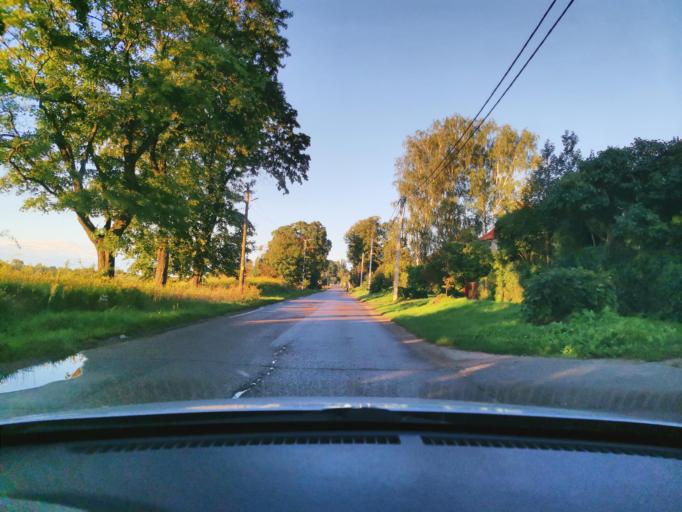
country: RU
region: Kaliningrad
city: Chernyakhovsk
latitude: 54.6551
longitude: 21.8230
